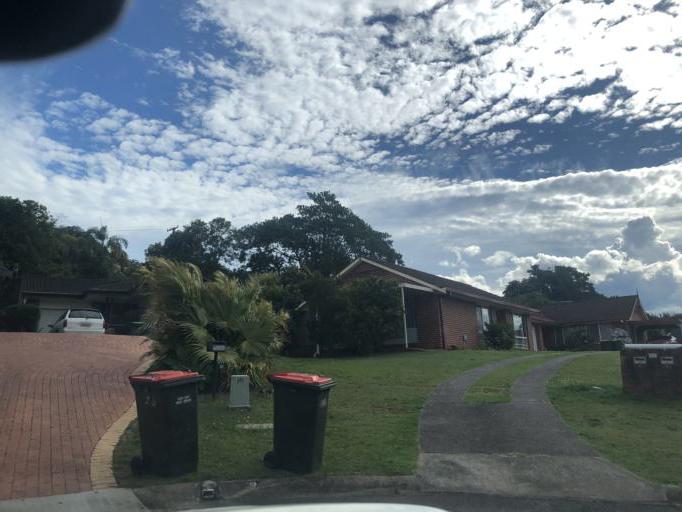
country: AU
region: New South Wales
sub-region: Coffs Harbour
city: Coffs Harbour
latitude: -30.2913
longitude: 153.0991
